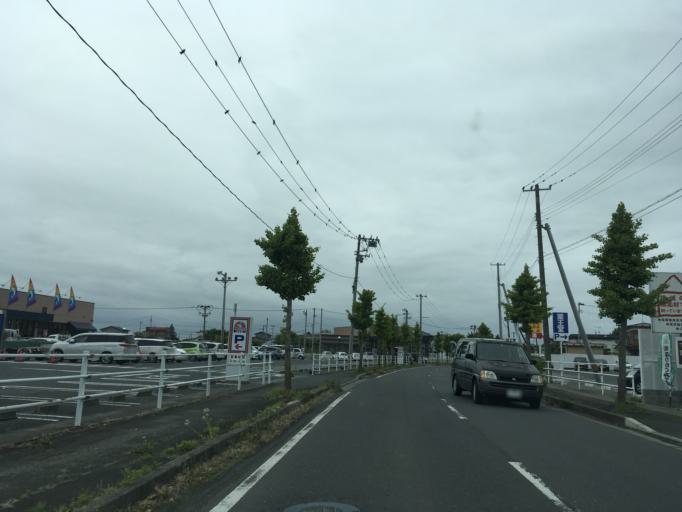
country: JP
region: Miyagi
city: Wakuya
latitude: 38.6801
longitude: 141.1924
